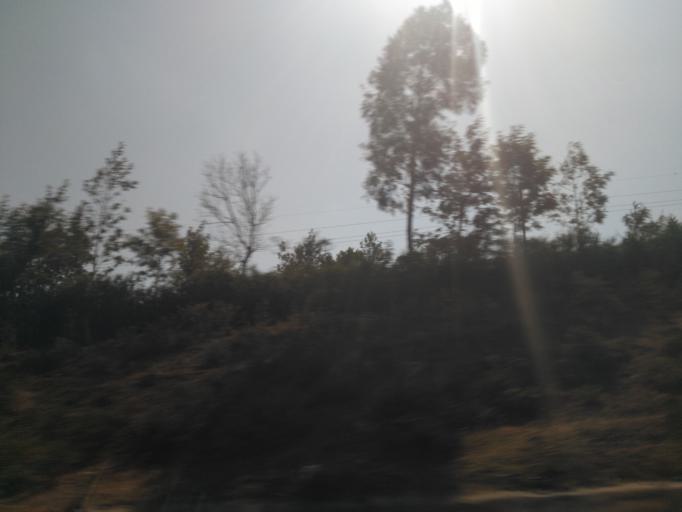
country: TZ
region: Arusha
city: Arusha
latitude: -3.2489
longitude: 36.6124
